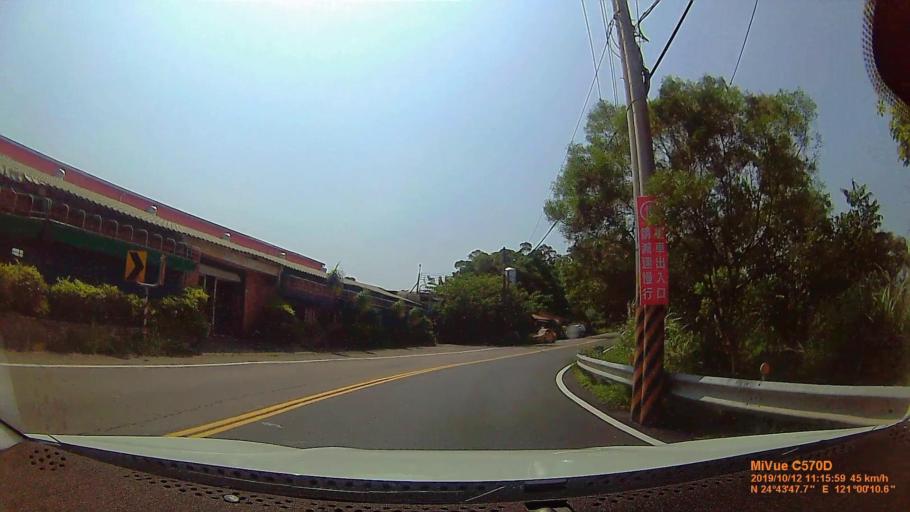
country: TW
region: Taiwan
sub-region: Hsinchu
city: Hsinchu
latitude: 24.7299
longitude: 121.0029
